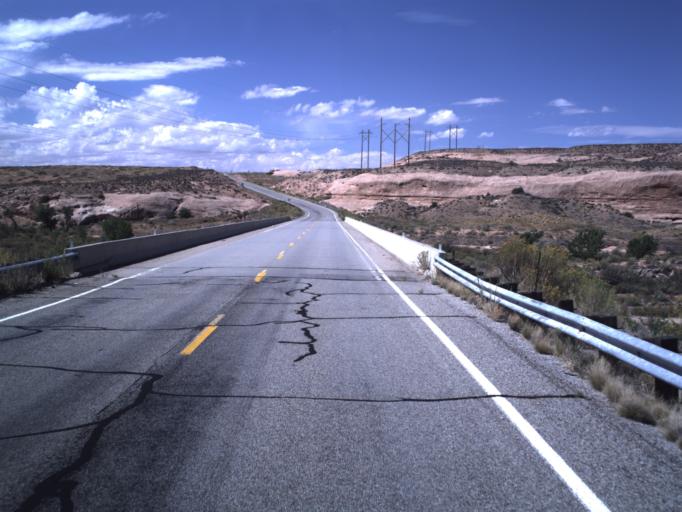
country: US
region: Utah
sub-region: San Juan County
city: Blanding
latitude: 37.3005
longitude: -109.4561
